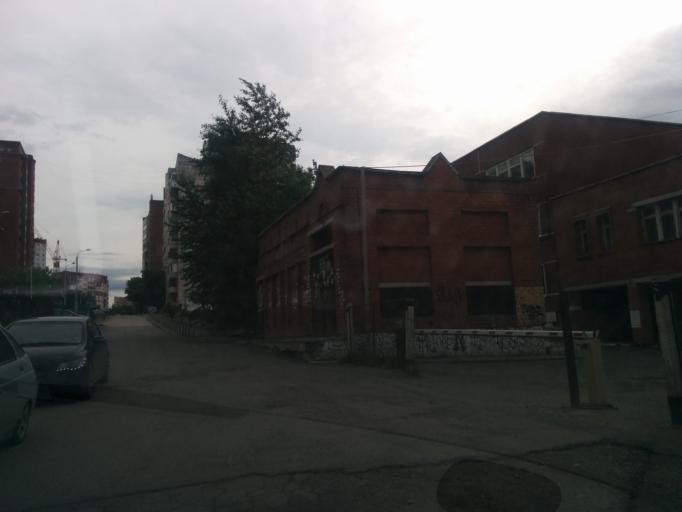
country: RU
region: Perm
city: Perm
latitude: 58.0095
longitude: 56.3026
